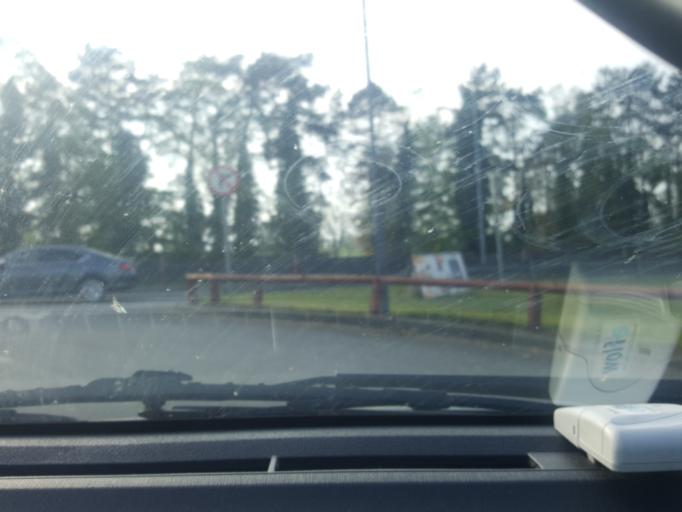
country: IE
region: Leinster
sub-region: Laois
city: Portlaoise
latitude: 53.0154
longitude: -7.3016
